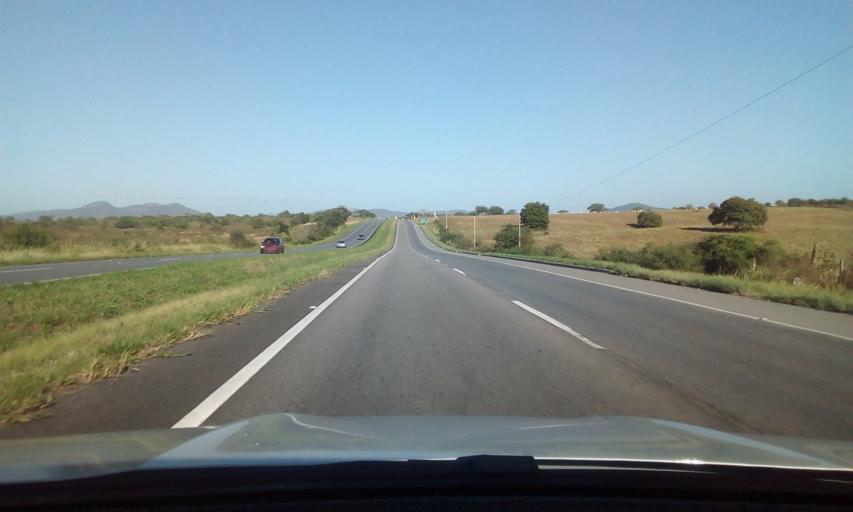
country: BR
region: Paraiba
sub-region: Pilar
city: Pilar
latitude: -7.1801
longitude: -35.3156
